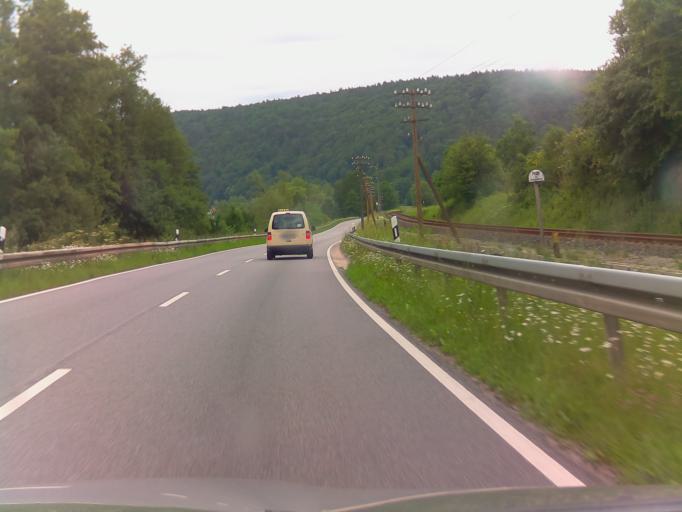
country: DE
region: Bavaria
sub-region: Regierungsbezirk Unterfranken
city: Grafendorf
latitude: 50.1153
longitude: 9.7329
